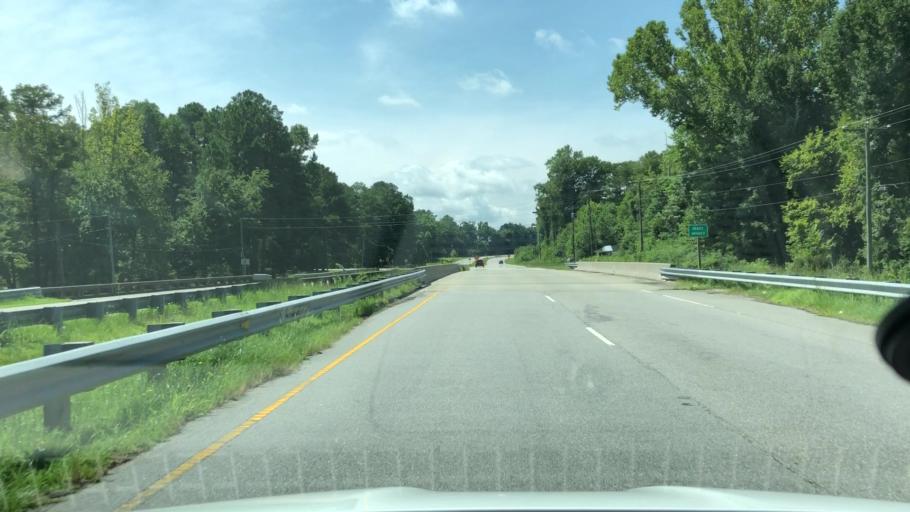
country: US
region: North Carolina
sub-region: Martin County
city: Williamston
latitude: 35.7894
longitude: -77.0593
